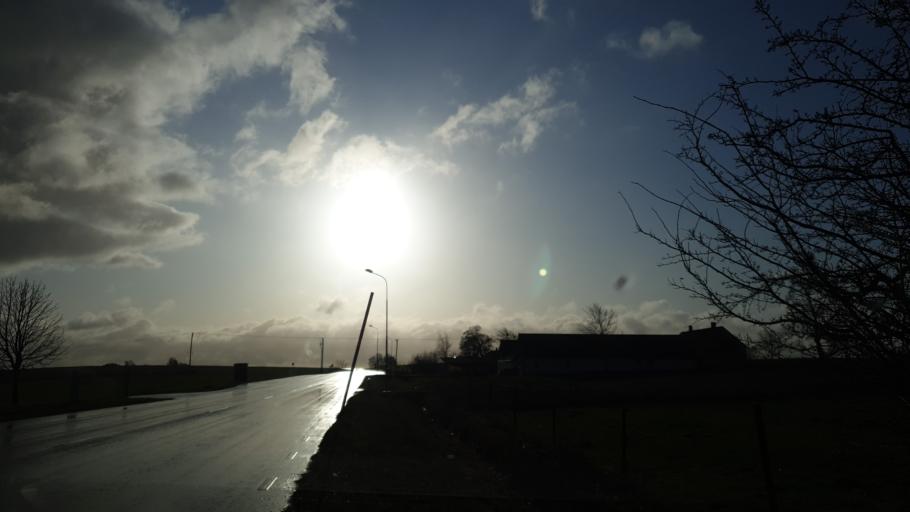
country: SE
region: Skane
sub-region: Skurups Kommun
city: Skivarp
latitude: 55.4499
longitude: 13.5464
